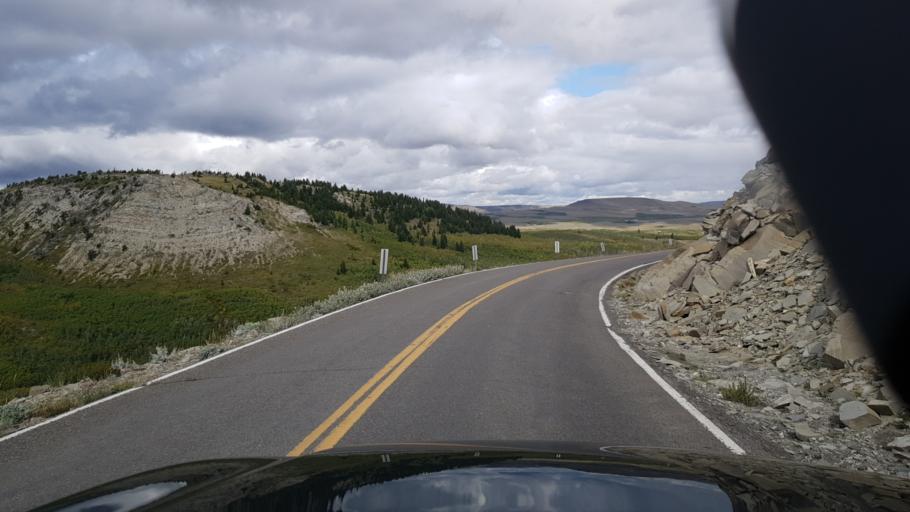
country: US
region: Montana
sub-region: Glacier County
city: South Browning
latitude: 48.5443
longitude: -113.2935
